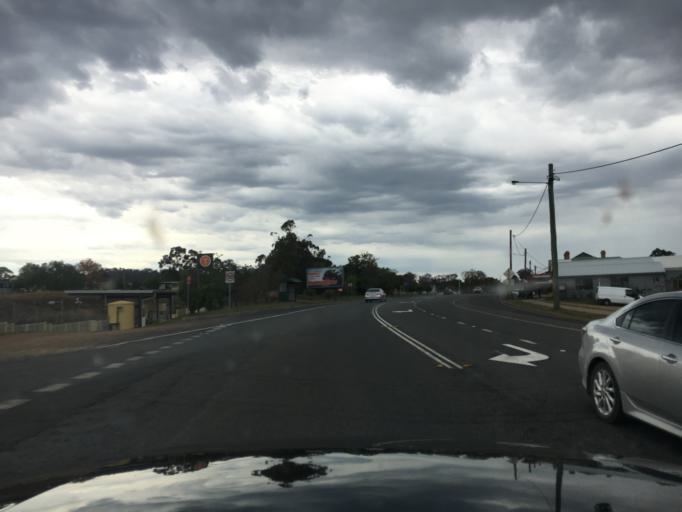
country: AU
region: New South Wales
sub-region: Muswellbrook
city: Muswellbrook
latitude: -32.1662
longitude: 150.8915
